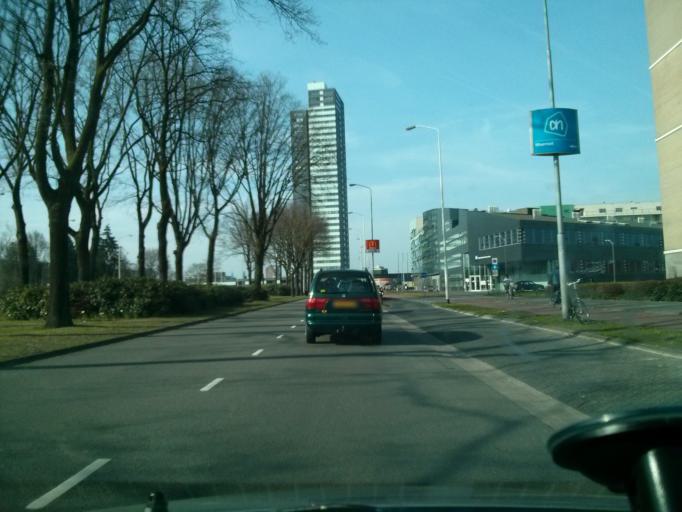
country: NL
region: North Brabant
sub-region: Gemeente Eindhoven
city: Eindhoven
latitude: 51.4652
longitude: 5.4754
